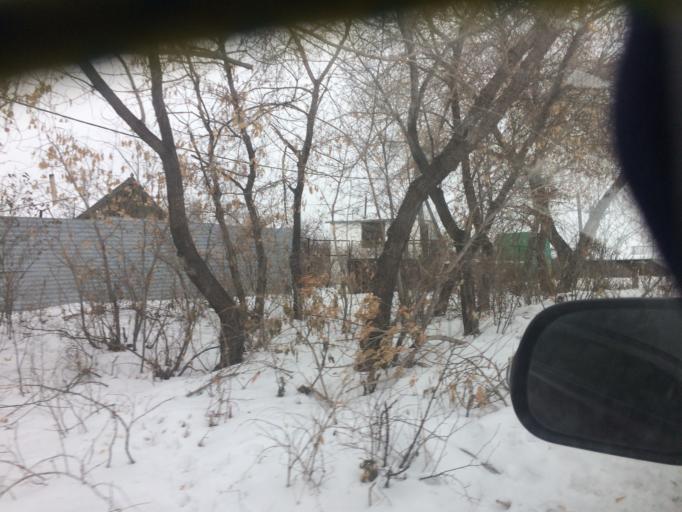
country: RU
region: Chelyabinsk
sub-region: Gorod Magnitogorsk
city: Magnitogorsk
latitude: 53.3581
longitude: 58.9826
